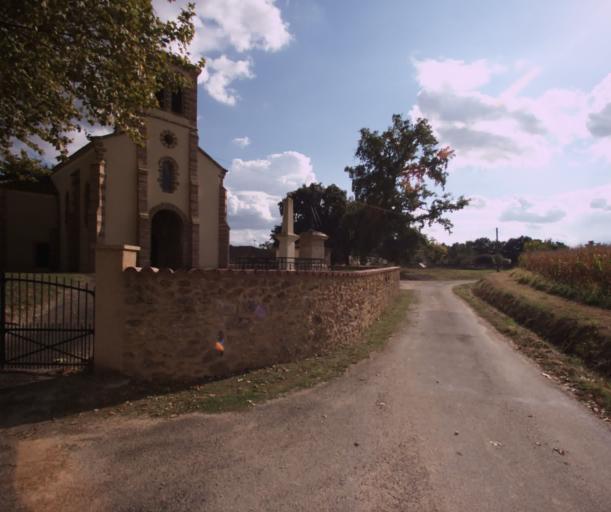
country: FR
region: Midi-Pyrenees
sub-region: Departement du Gers
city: Cazaubon
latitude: 43.9069
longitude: -0.0512
